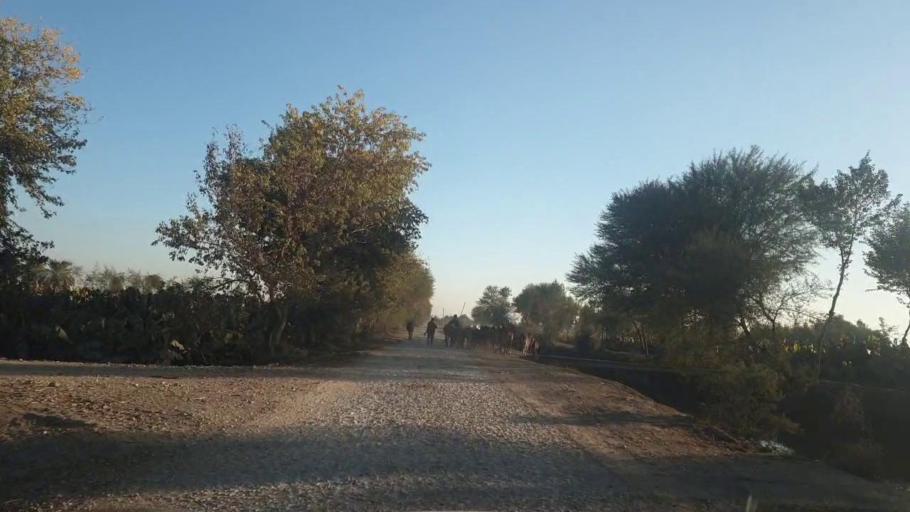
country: PK
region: Sindh
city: Ghotki
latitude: 28.0066
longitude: 69.2696
